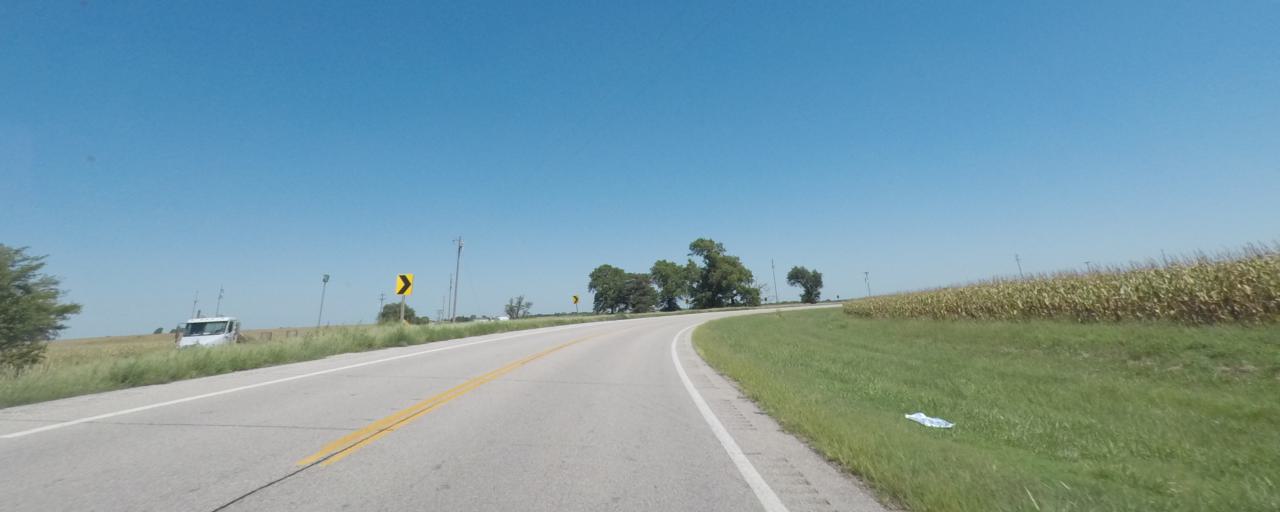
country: US
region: Kansas
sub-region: Sumner County
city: Belle Plaine
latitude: 37.3889
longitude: -97.3849
